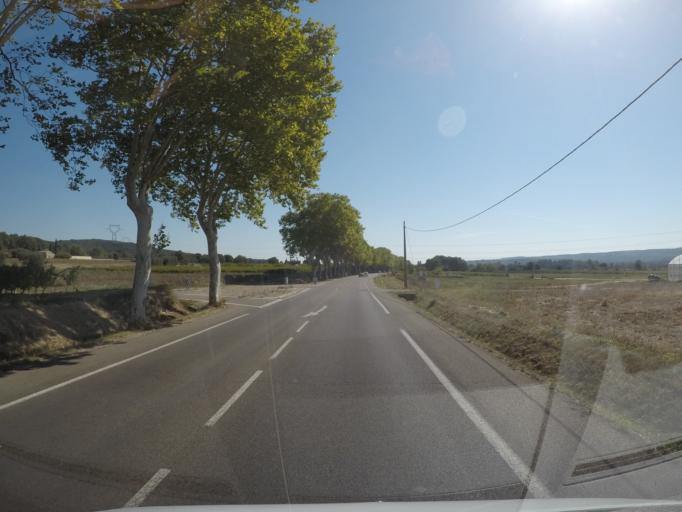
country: FR
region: Languedoc-Roussillon
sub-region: Departement du Gard
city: Uzes
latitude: 43.9848
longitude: 4.4600
